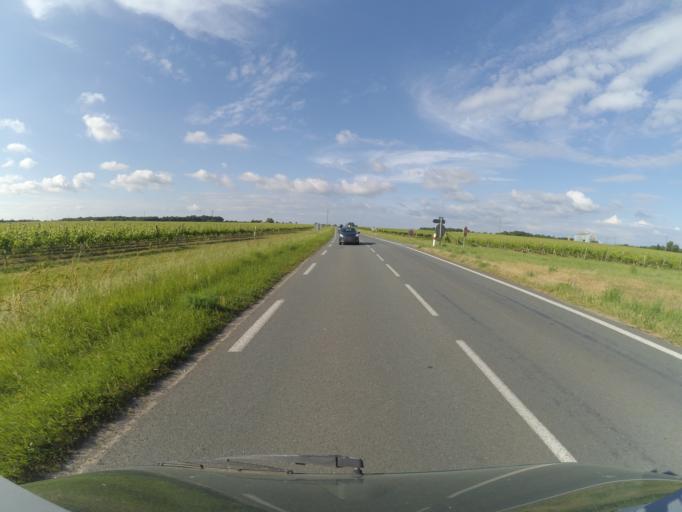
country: FR
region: Poitou-Charentes
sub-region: Departement de la Charente-Maritime
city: Le Gua
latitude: 45.7372
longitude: -0.9515
